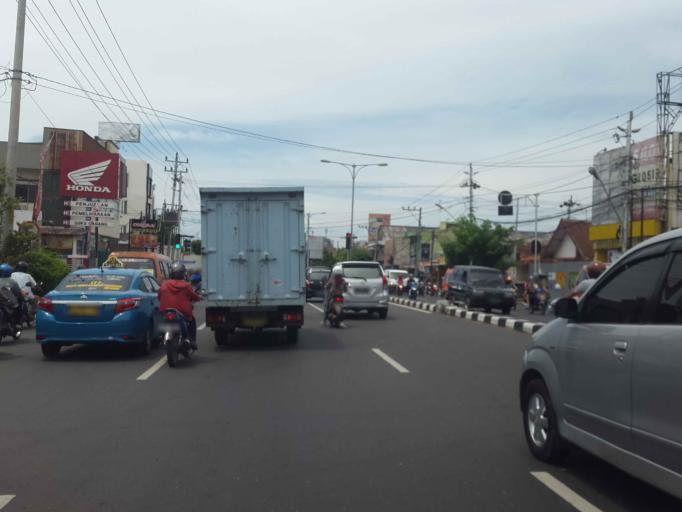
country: ID
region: Central Java
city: Semarang
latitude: -6.9985
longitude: 110.4420
